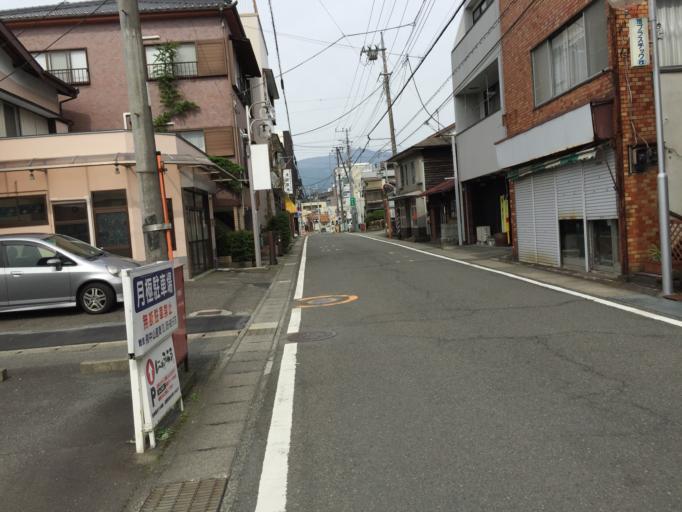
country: JP
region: Shizuoka
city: Mishima
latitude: 35.1720
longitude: 138.9111
